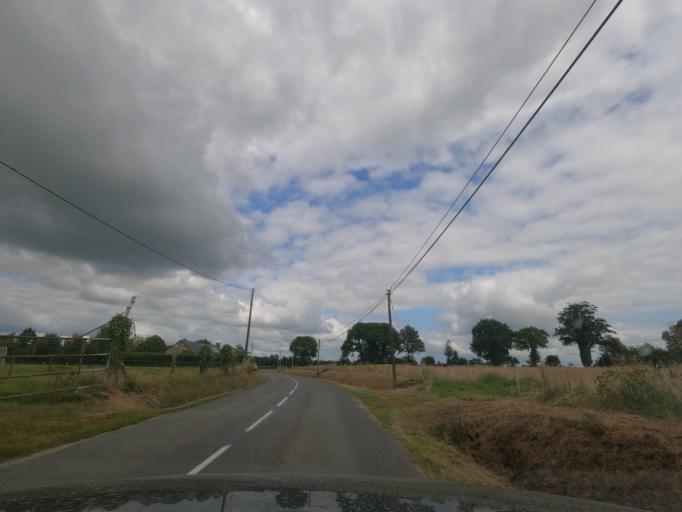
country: FR
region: Lower Normandy
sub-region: Departement de la Manche
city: Le Teilleul
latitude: 48.5166
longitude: -0.8958
